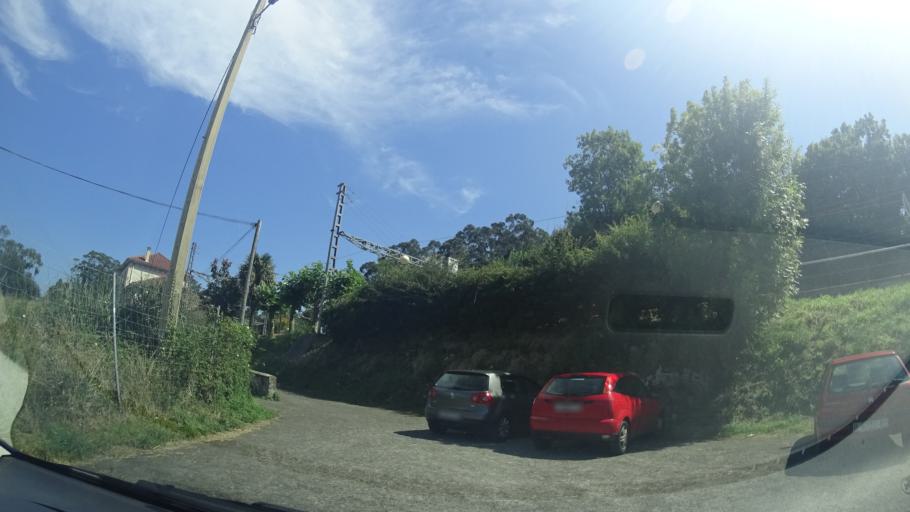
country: ES
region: Asturias
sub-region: Province of Asturias
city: Ribadesella
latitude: 43.4596
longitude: -5.0555
